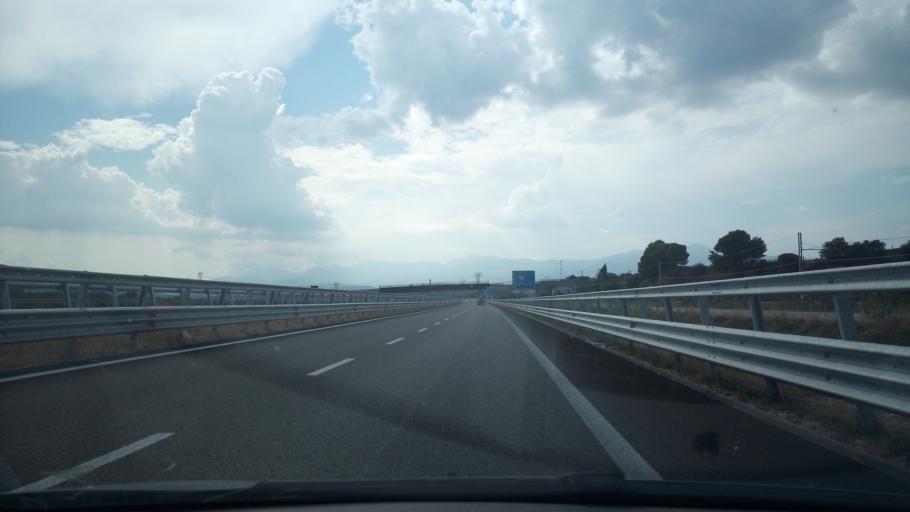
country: IT
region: Calabria
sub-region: Provincia di Cosenza
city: Doria
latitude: 39.7270
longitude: 16.3324
